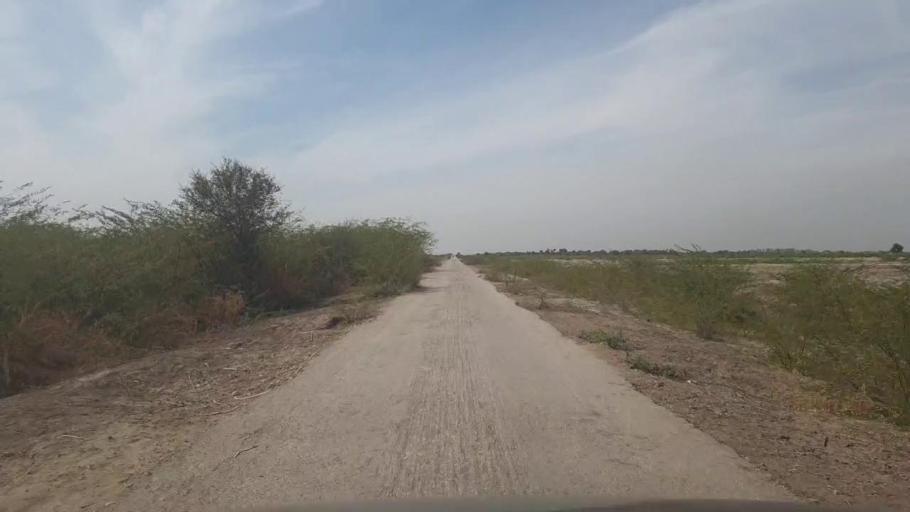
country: PK
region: Sindh
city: Kunri
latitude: 25.2121
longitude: 69.6173
